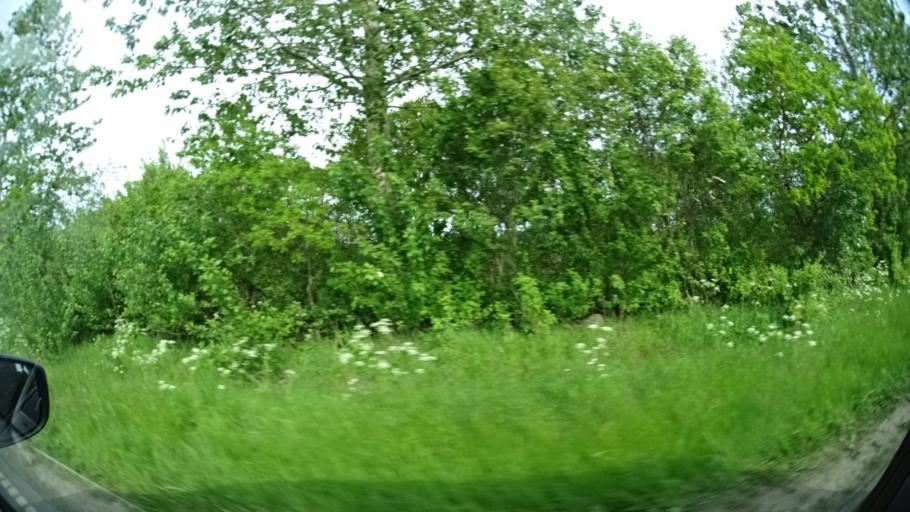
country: DK
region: Central Jutland
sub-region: Arhus Kommune
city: Malling
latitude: 56.0549
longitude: 10.1934
